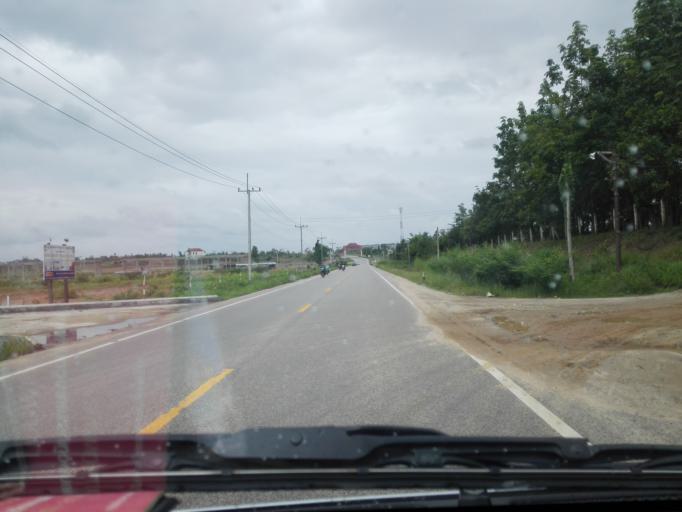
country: TH
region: Tak
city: Mae Sot
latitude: 16.6955
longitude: 98.4162
